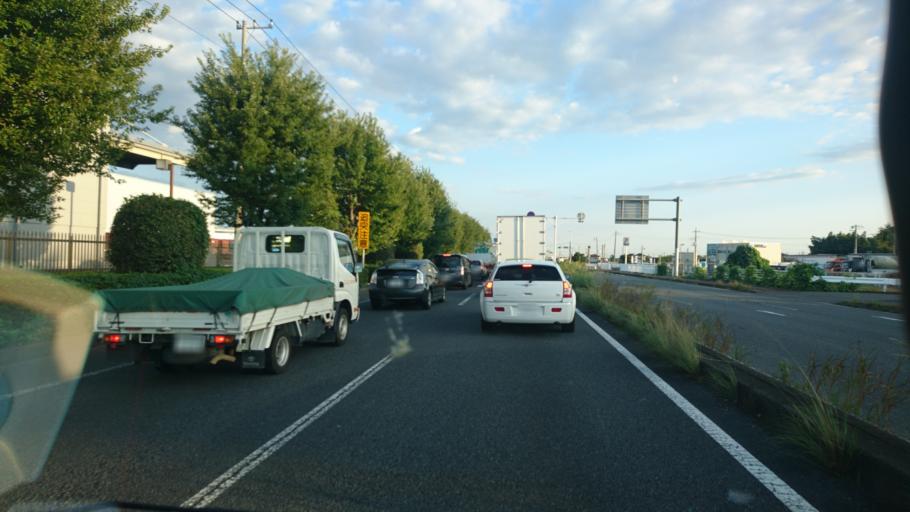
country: JP
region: Gunma
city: Ota
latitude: 36.3435
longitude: 139.3838
